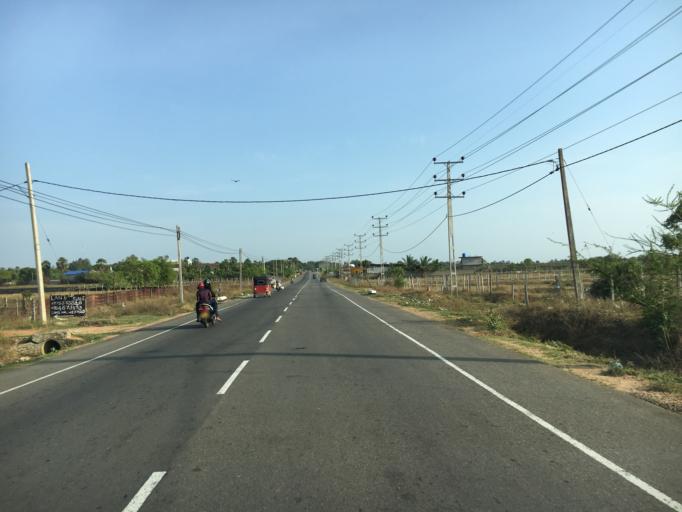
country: LK
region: Eastern Province
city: Eravur Town
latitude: 7.9353
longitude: 81.5102
